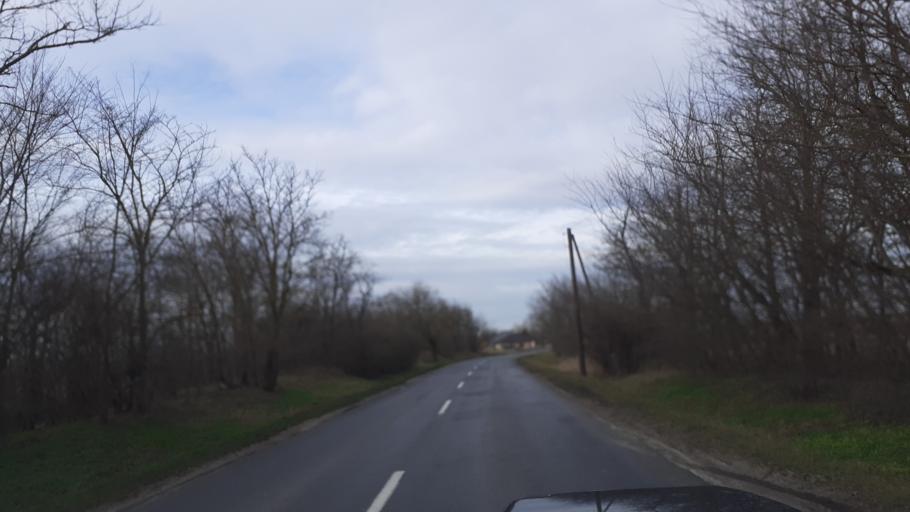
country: HU
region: Fejer
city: Szabadbattyan
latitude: 47.0734
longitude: 18.4152
